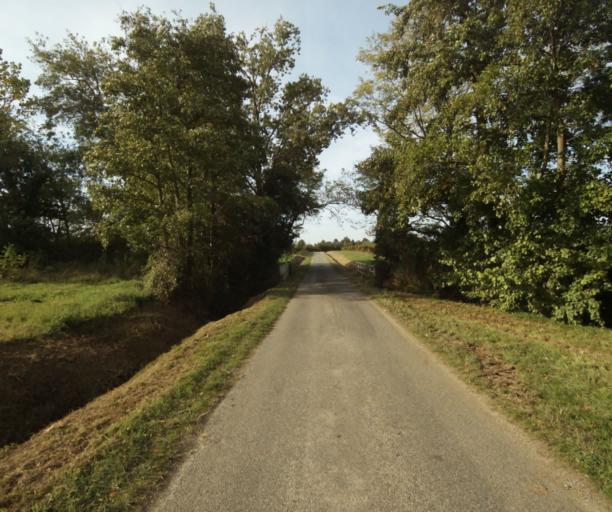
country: FR
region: Midi-Pyrenees
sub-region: Departement du Tarn-et-Garonne
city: Campsas
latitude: 43.9052
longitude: 1.3207
